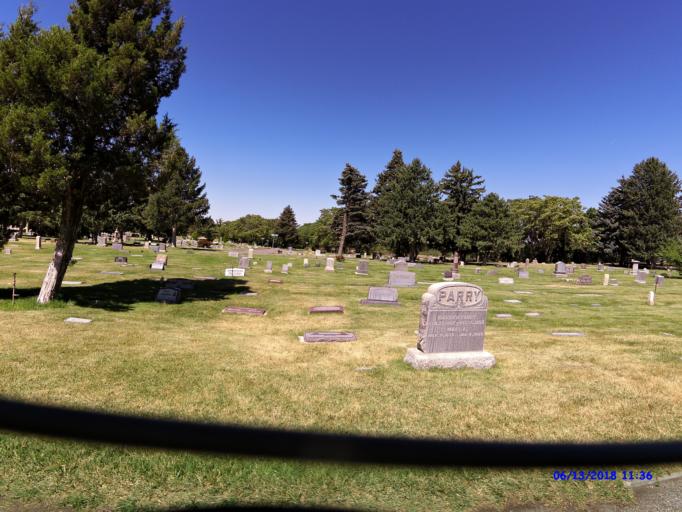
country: US
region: Utah
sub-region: Weber County
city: Ogden
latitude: 41.2333
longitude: -111.9639
